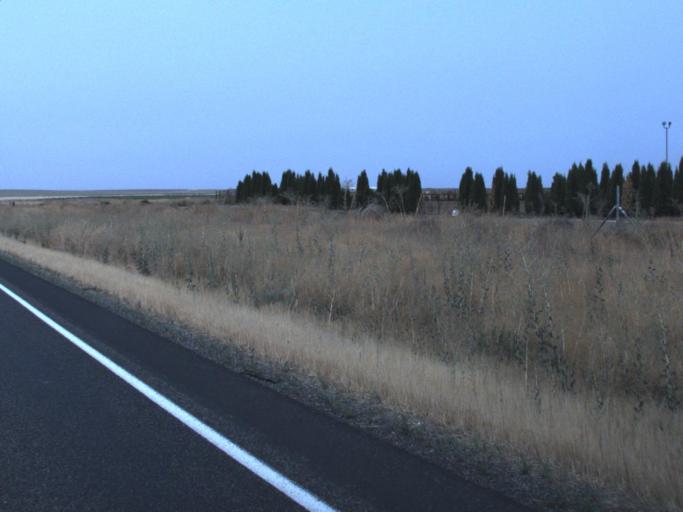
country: US
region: Oregon
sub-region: Morrow County
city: Irrigon
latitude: 46.0061
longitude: -119.6028
